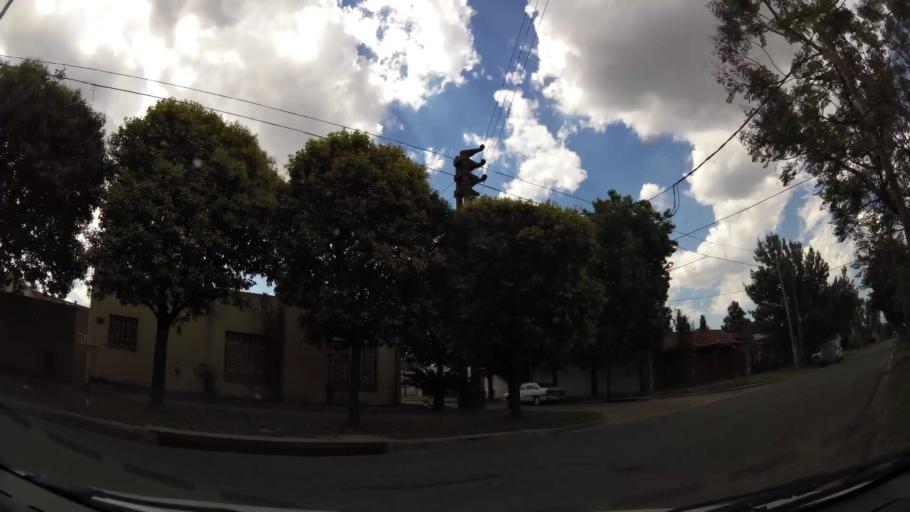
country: AR
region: Buenos Aires
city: Ituzaingo
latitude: -34.6463
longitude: -58.6768
